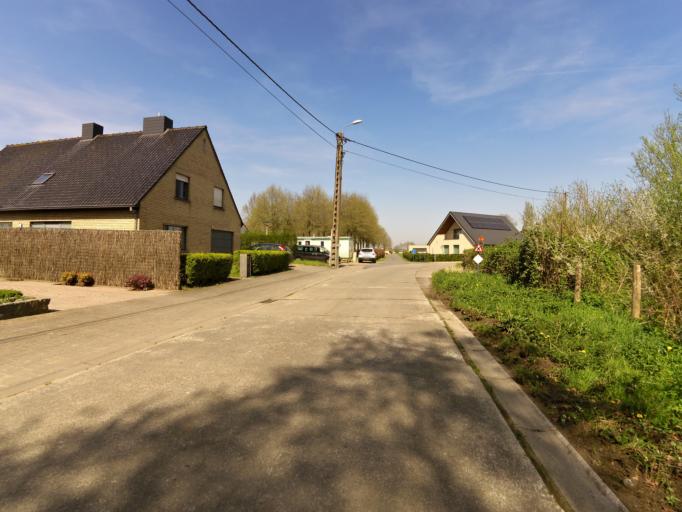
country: BE
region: Flanders
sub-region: Provincie West-Vlaanderen
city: Koekelare
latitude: 51.0915
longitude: 2.9851
